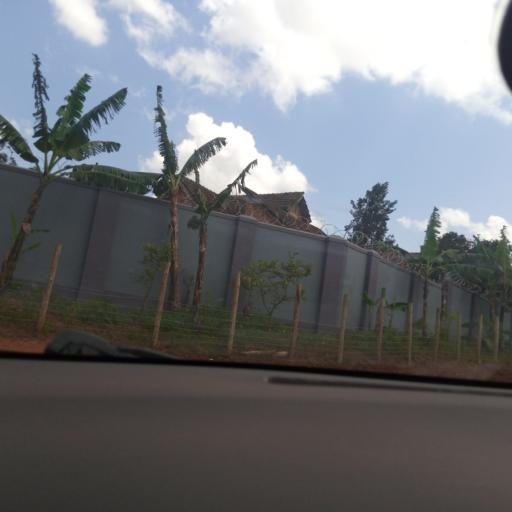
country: UG
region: Central Region
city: Masaka
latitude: -0.3299
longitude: 31.7425
